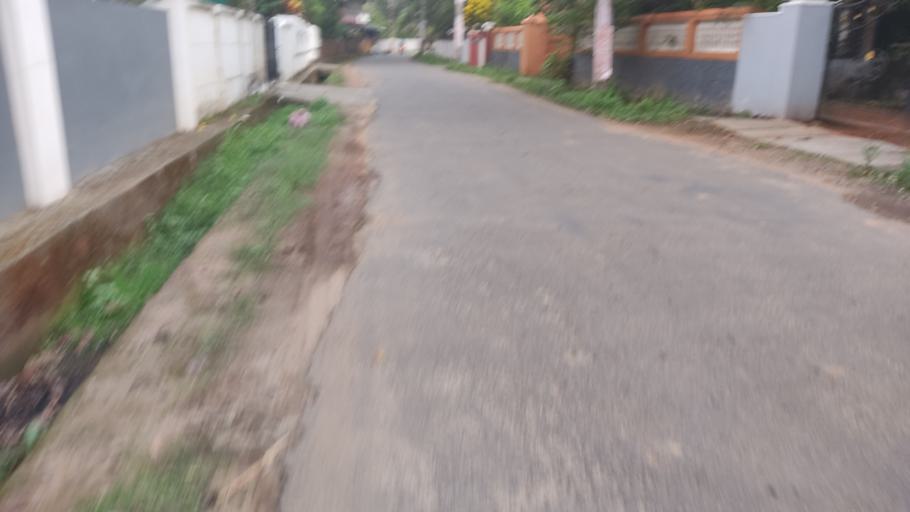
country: IN
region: Kerala
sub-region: Thrissur District
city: Irinjalakuda
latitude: 10.4267
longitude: 76.2858
